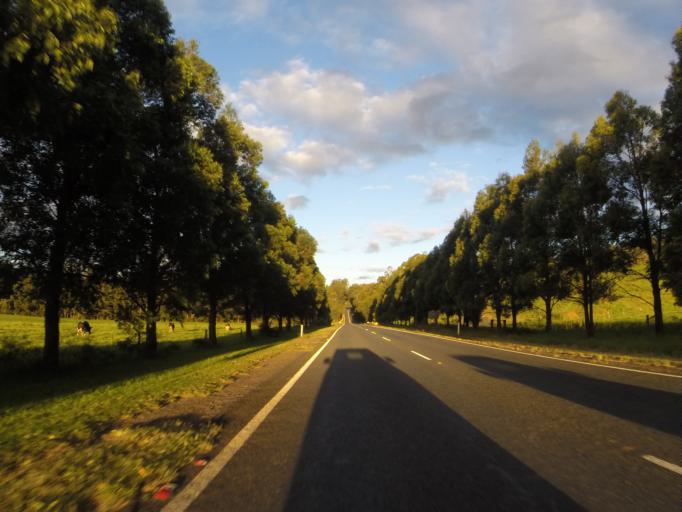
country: AU
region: New South Wales
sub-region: Shellharbour
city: Calderwood
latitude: -34.5789
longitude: 150.7000
